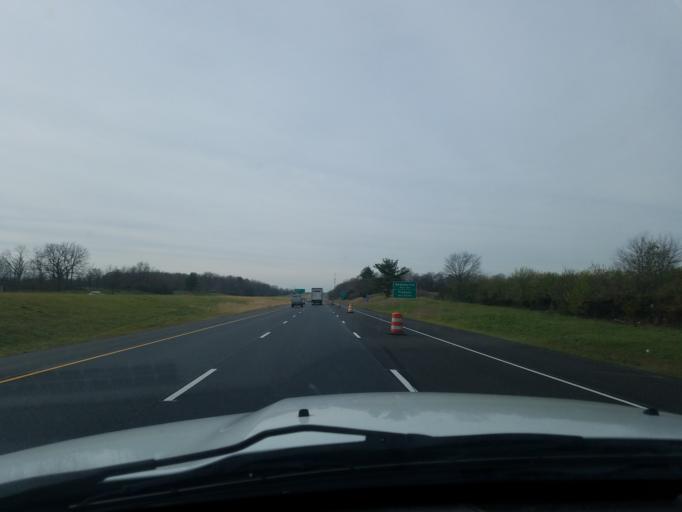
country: US
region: Indiana
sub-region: Hancock County
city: Fortville
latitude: 39.9914
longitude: -85.8934
